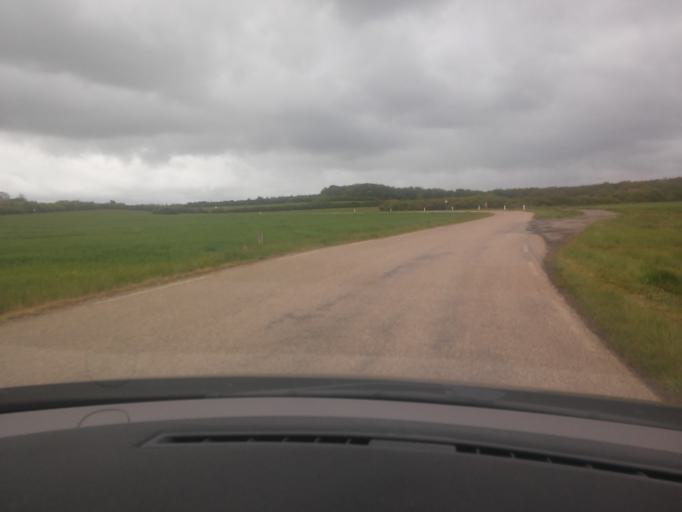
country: FR
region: Lorraine
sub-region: Departement de la Moselle
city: Mecleuves
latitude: 49.0324
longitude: 6.2436
